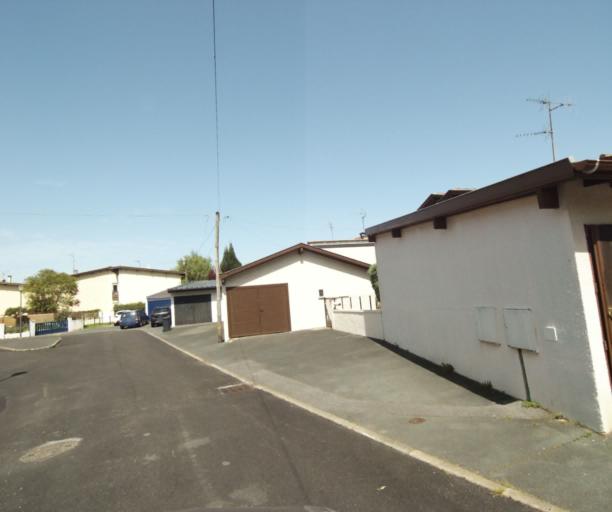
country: FR
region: Aquitaine
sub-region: Departement des Pyrenees-Atlantiques
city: Bayonne
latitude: 43.4761
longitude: -1.4581
